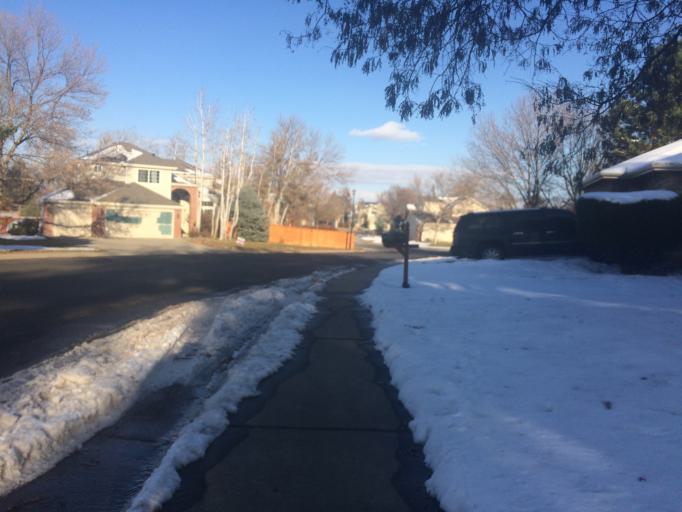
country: US
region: Colorado
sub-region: Boulder County
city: Louisville
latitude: 39.9949
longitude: -105.1227
